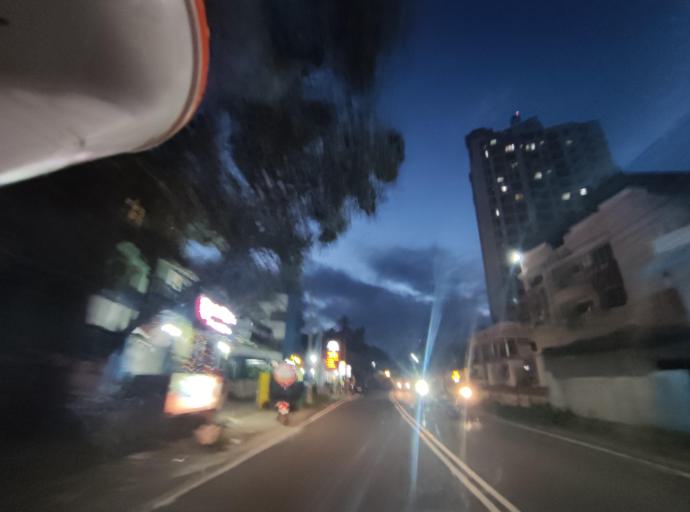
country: IN
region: Kerala
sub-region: Thiruvananthapuram
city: Thiruvananthapuram
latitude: 8.5419
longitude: 76.9616
